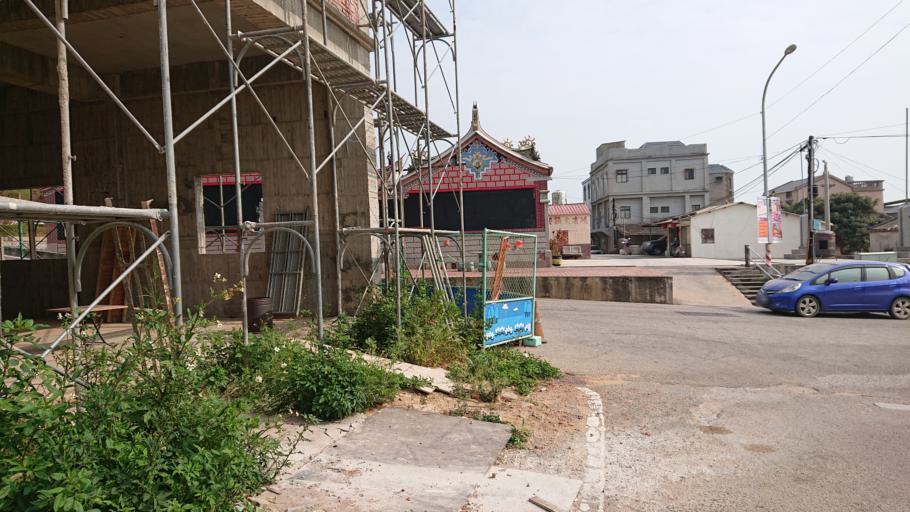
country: TW
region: Fukien
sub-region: Kinmen
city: Jincheng
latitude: 24.4303
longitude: 118.2479
